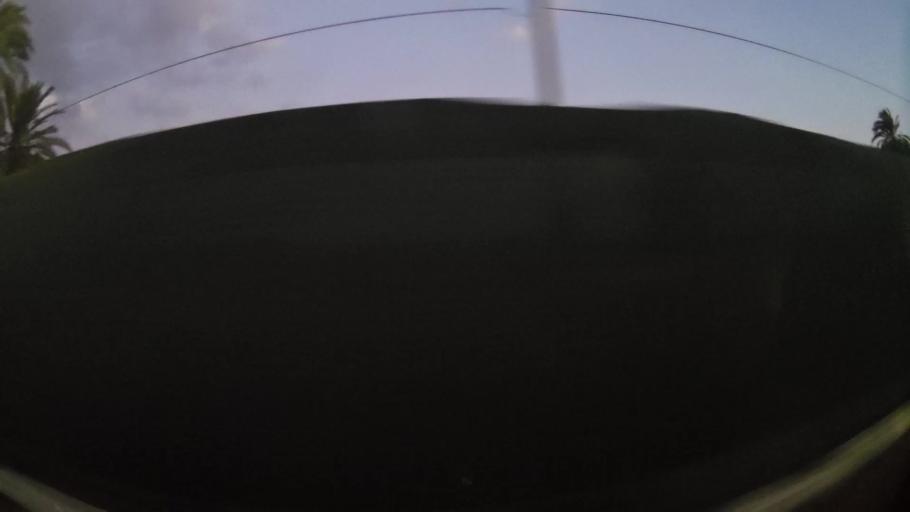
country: CY
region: Lefkosia
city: Nicosia
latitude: 35.1891
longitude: 33.3728
